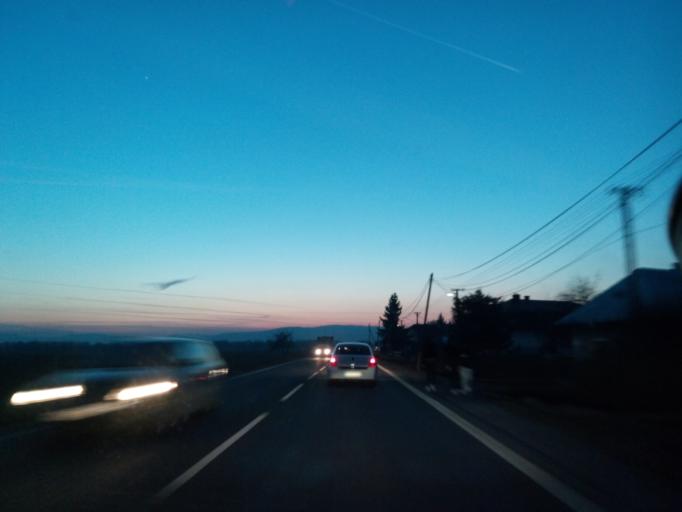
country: SK
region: Kosicky
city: Trebisov
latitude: 48.6988
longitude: 21.7949
